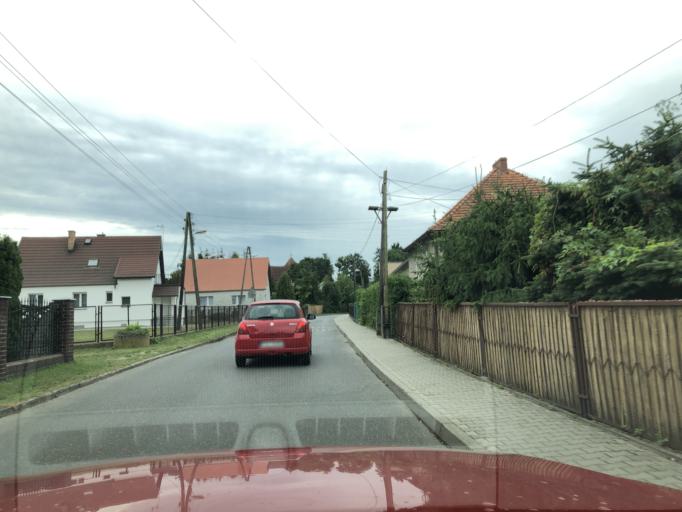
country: PL
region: Greater Poland Voivodeship
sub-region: Powiat szamotulski
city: Pniewy
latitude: 52.5116
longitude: 16.2512
